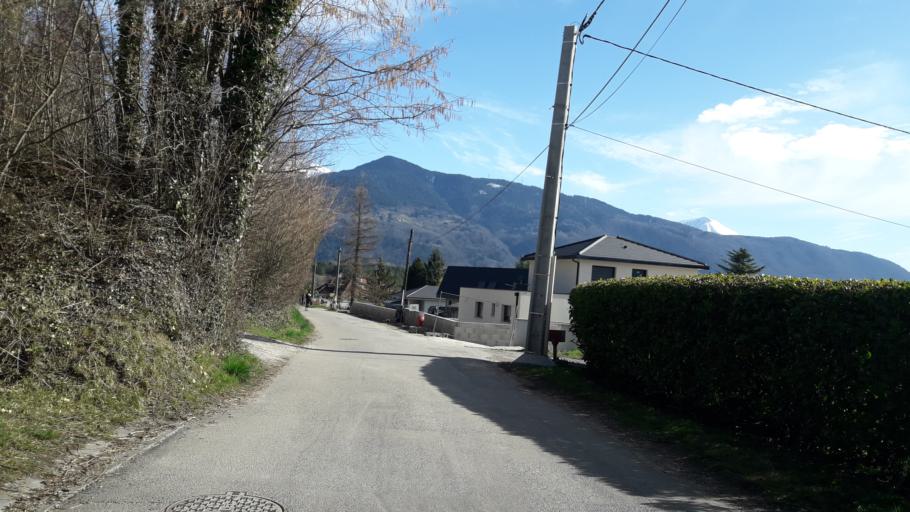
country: FR
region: Rhone-Alpes
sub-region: Departement de l'Isere
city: Herbeys
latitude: 45.1320
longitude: 5.7962
